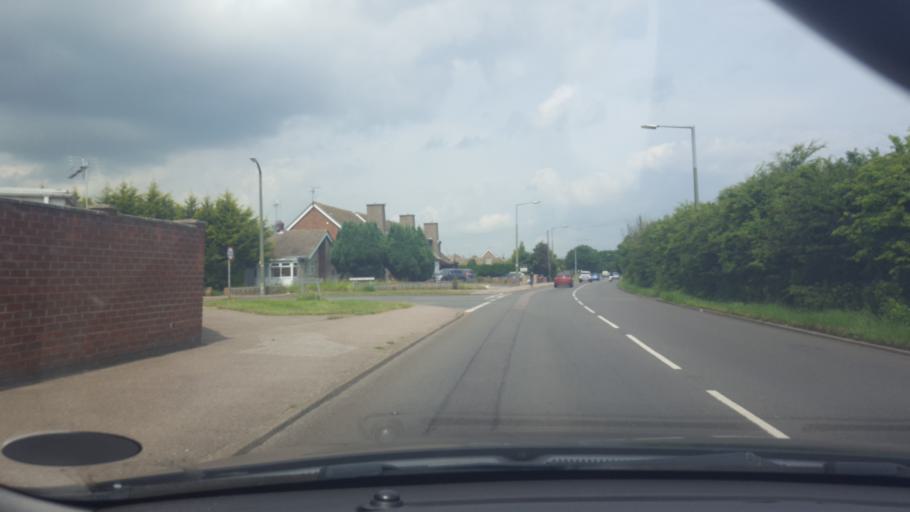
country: GB
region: England
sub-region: Essex
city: Clacton-on-Sea
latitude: 51.7859
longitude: 1.1197
